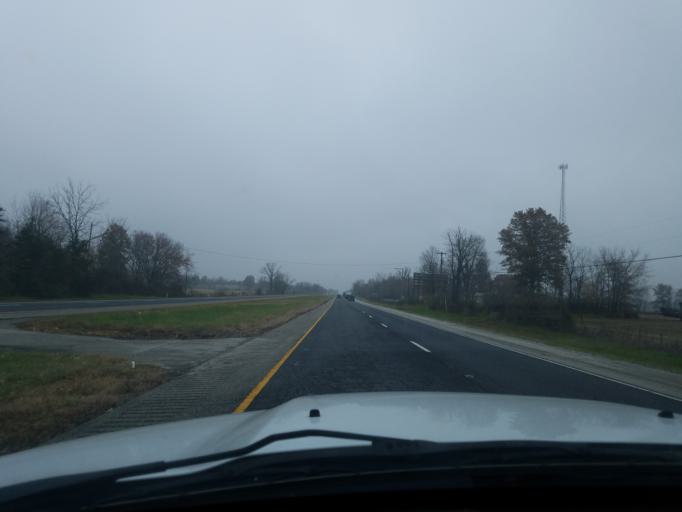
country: US
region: Indiana
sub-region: Hamilton County
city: Westfield
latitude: 40.1204
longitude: -86.1280
